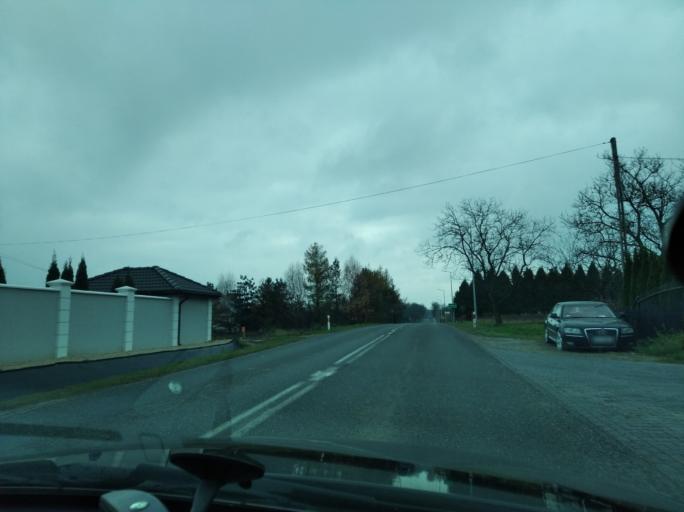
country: PL
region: Subcarpathian Voivodeship
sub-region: Powiat przeworski
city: Sietesz
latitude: 50.0061
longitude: 22.3465
